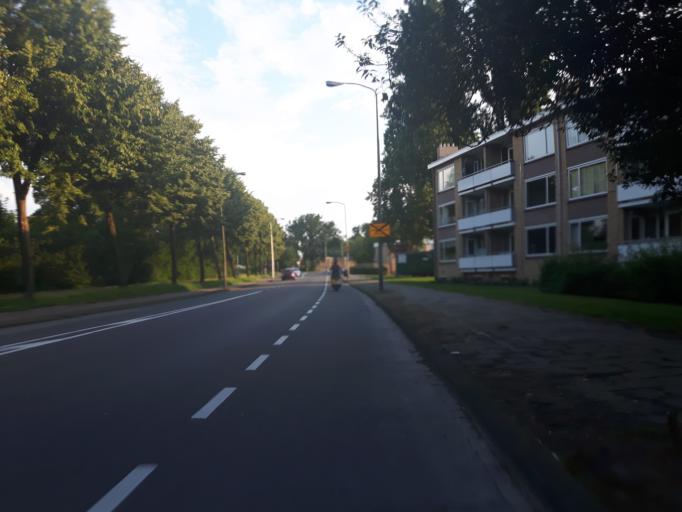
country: NL
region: Overijssel
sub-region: Gemeente Hengelo
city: Hengelo
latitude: 52.2522
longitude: 6.8041
